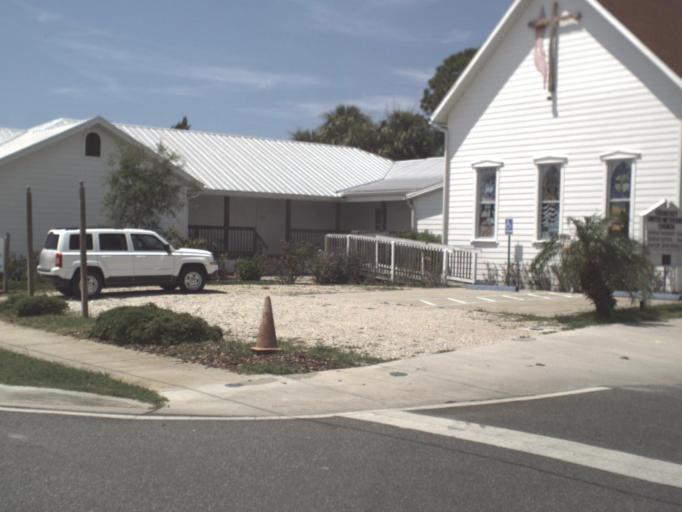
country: US
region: Florida
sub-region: Levy County
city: Chiefland
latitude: 29.1374
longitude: -83.0341
